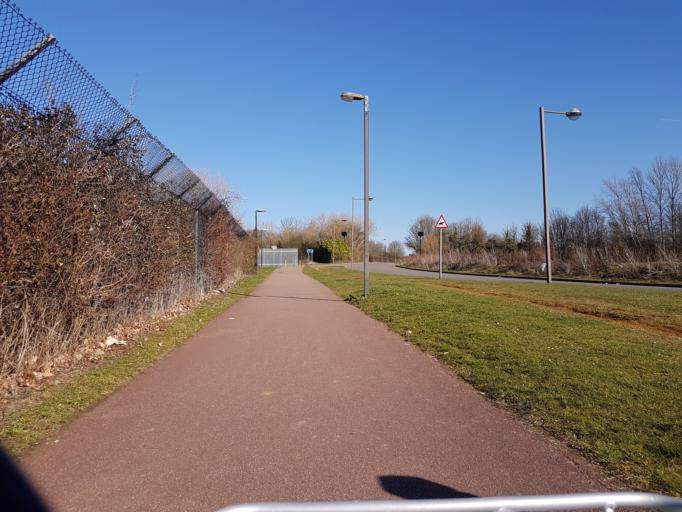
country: GB
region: England
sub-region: Milton Keynes
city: Milton Keynes
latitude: 52.0172
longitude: -0.7594
